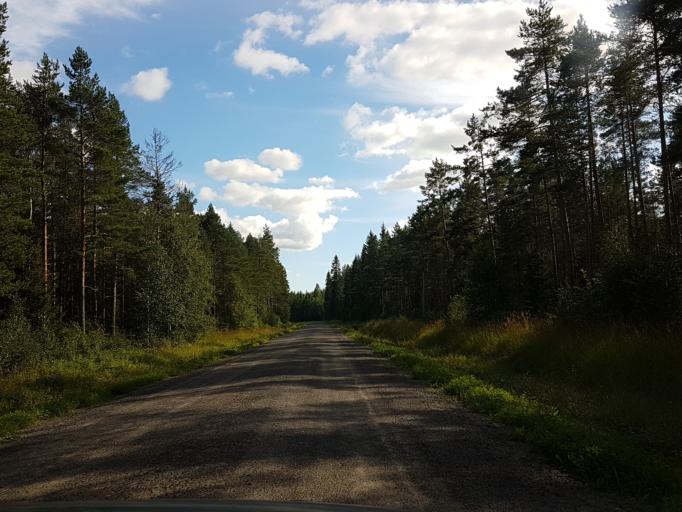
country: SE
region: Vaesterbotten
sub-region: Robertsfors Kommun
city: Robertsfors
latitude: 64.1728
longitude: 20.6458
